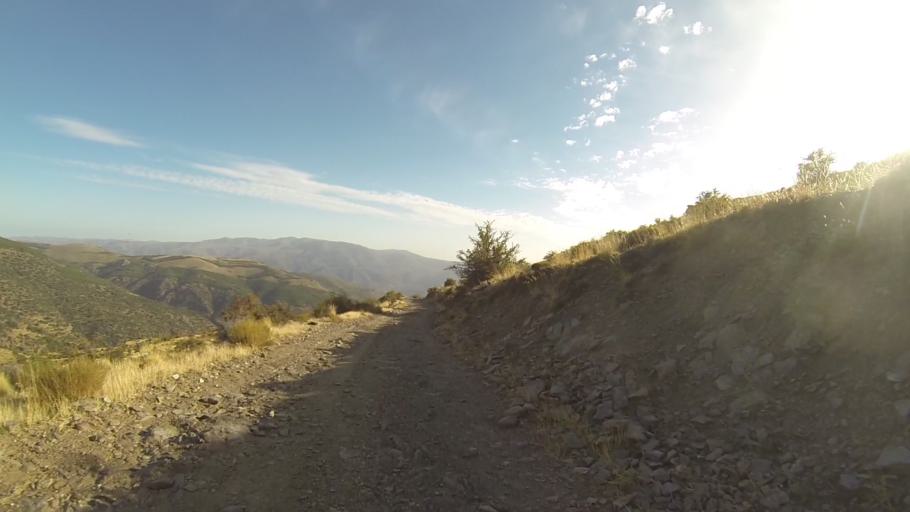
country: ES
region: Andalusia
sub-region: Provincia de Almeria
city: Laujar de Andarax
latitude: 37.0674
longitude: -2.8866
